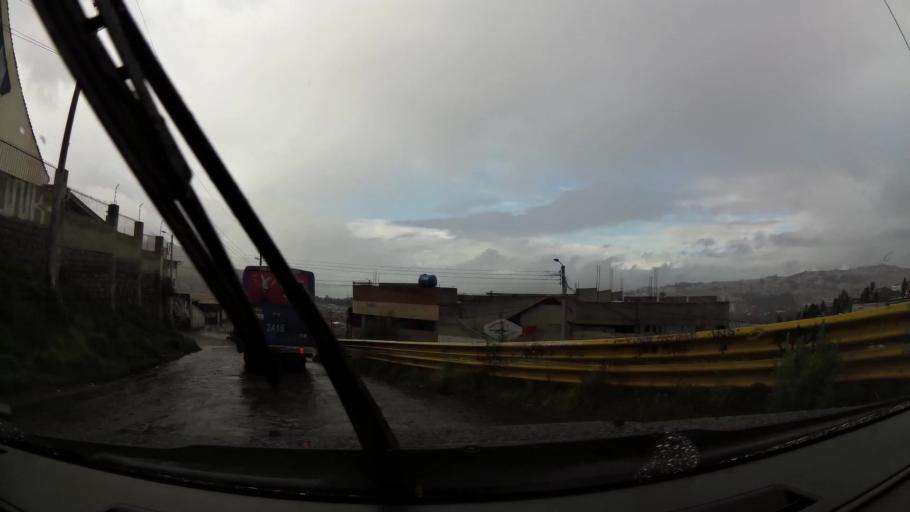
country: EC
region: Pichincha
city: Quito
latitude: -0.0875
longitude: -78.5105
